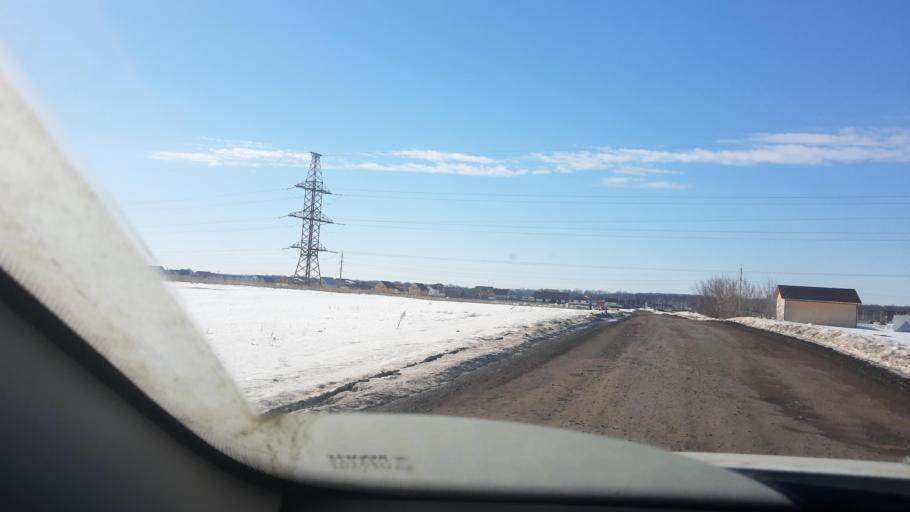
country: RU
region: Bashkortostan
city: Kabakovo
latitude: 54.5658
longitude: 56.0435
